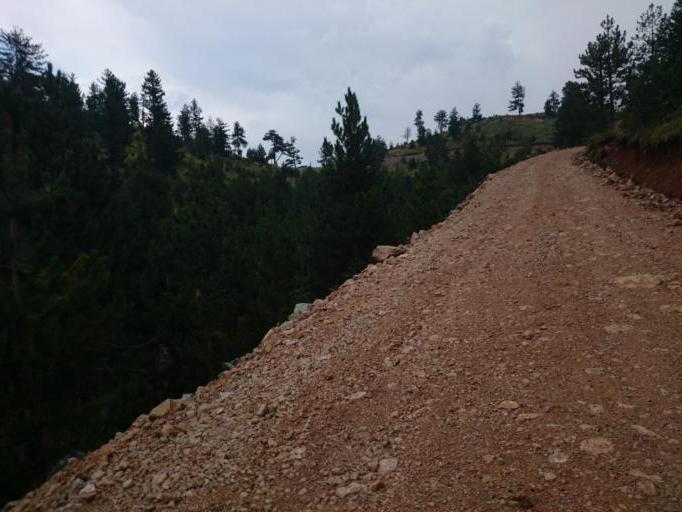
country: AL
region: Diber
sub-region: Rrethi i Dibres
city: Fushe-Lure
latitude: 41.7750
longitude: 20.2226
